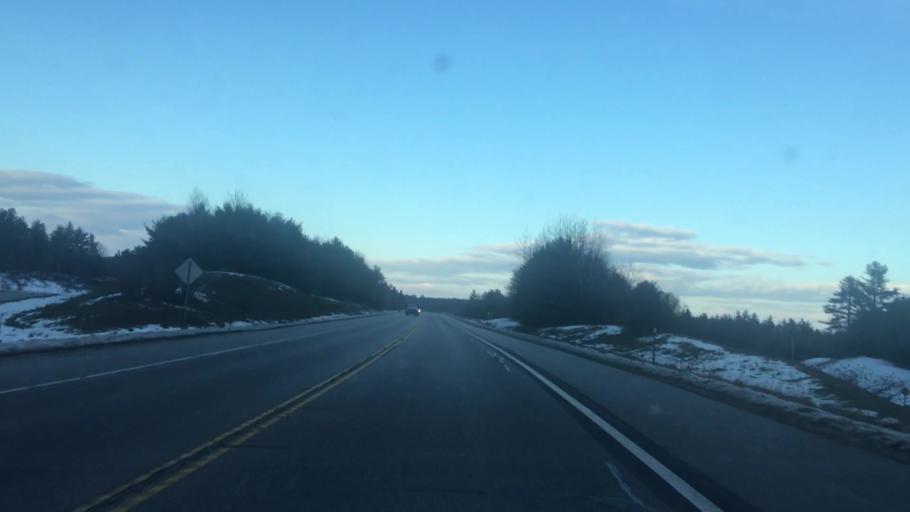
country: US
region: New Hampshire
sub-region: Hillsborough County
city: Hillsboro
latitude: 43.1332
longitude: -71.8824
